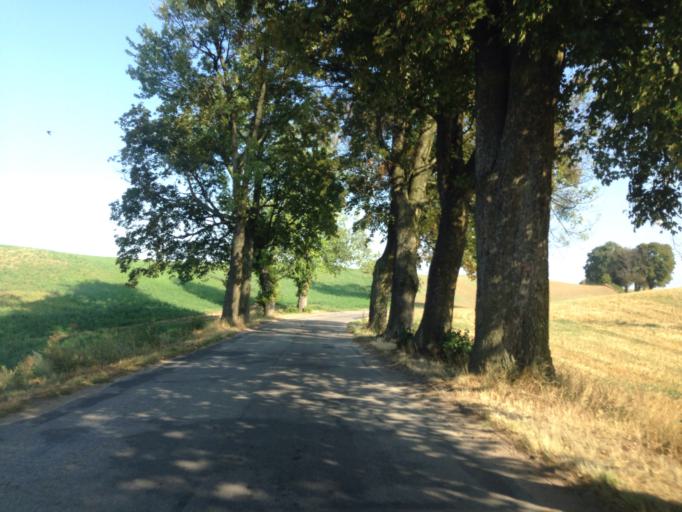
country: PL
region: Kujawsko-Pomorskie
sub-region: Powiat brodnicki
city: Brzozie
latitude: 53.3133
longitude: 19.6061
